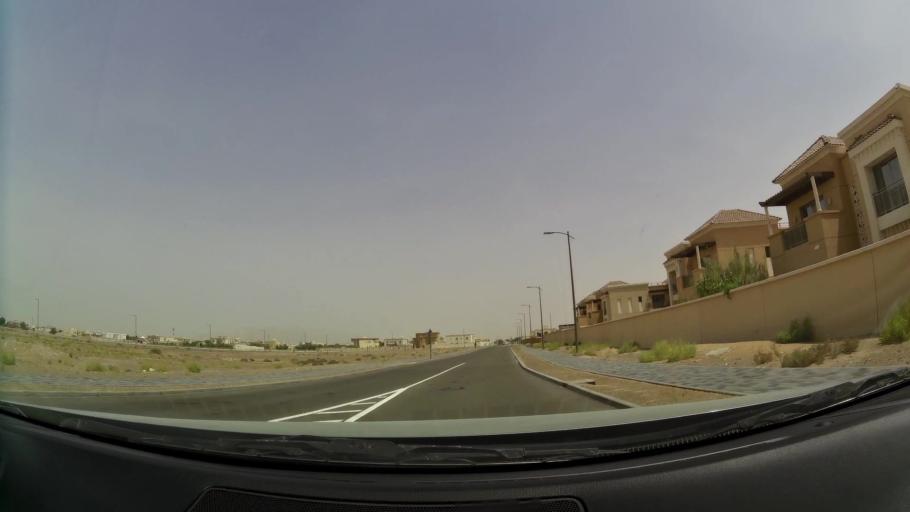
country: AE
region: Abu Dhabi
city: Al Ain
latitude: 24.1508
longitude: 55.6378
